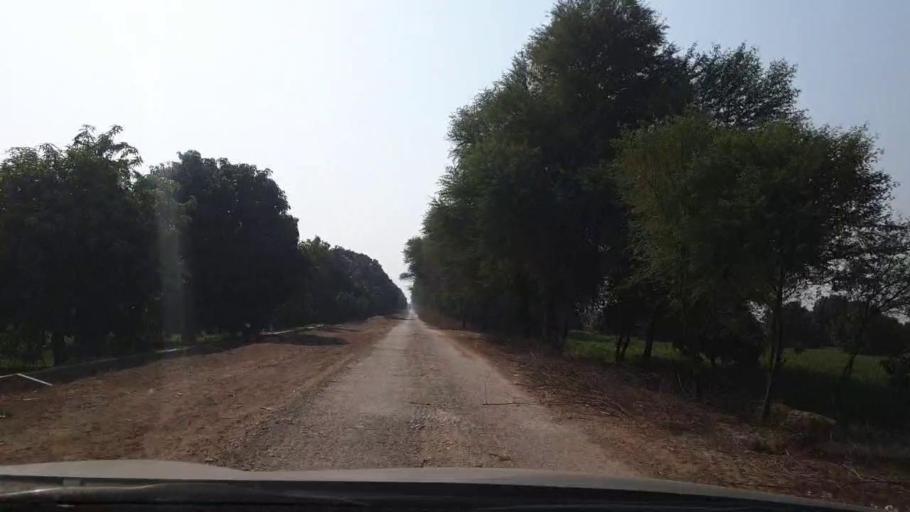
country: PK
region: Sindh
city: Tando Allahyar
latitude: 25.5165
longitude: 68.7861
